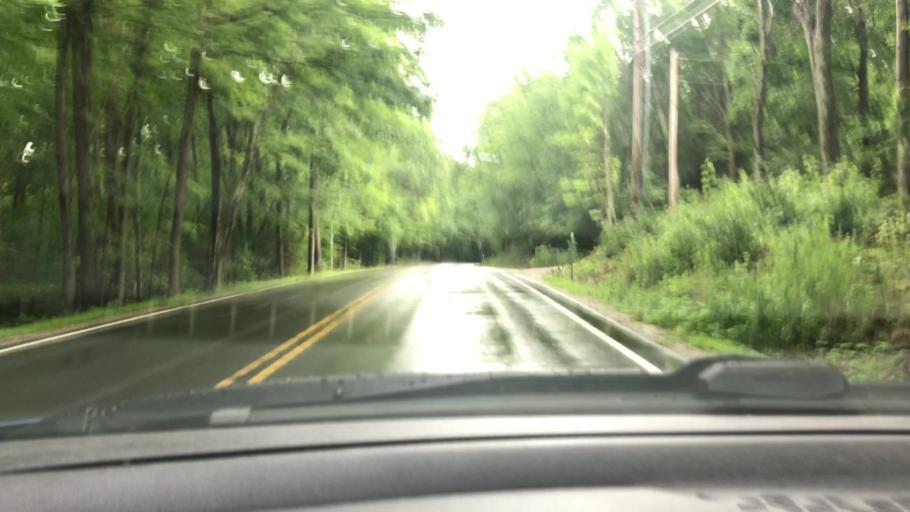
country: US
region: New Hampshire
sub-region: Merrimack County
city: Epsom
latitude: 43.2047
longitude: -71.2754
